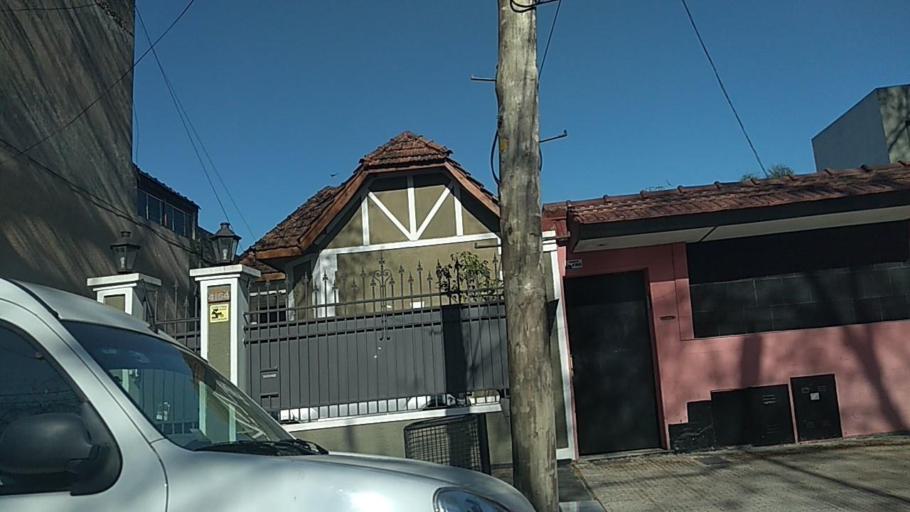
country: AR
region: Buenos Aires F.D.
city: Villa Santa Rita
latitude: -34.6064
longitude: -58.5083
